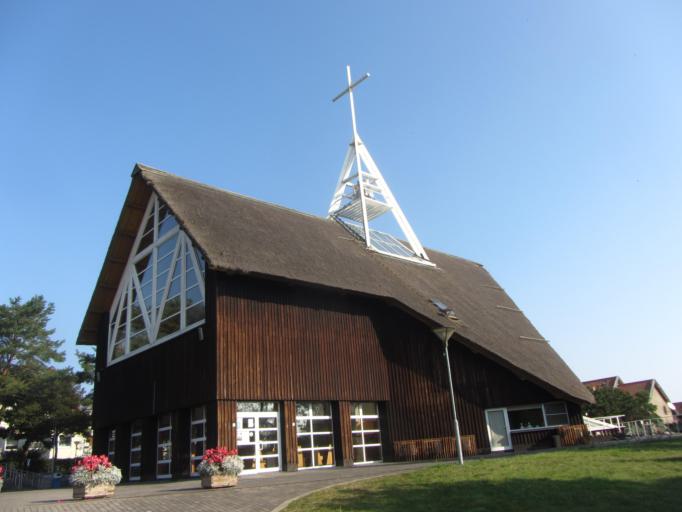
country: LT
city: Nida
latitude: 55.3023
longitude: 21.0014
